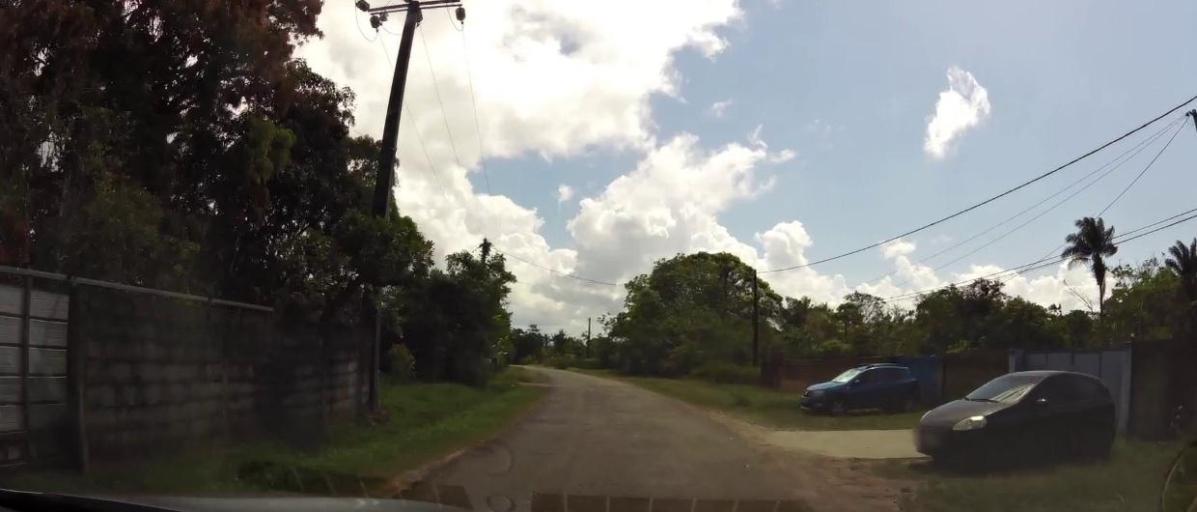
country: GF
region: Guyane
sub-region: Guyane
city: Matoury
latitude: 4.8317
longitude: -52.3097
